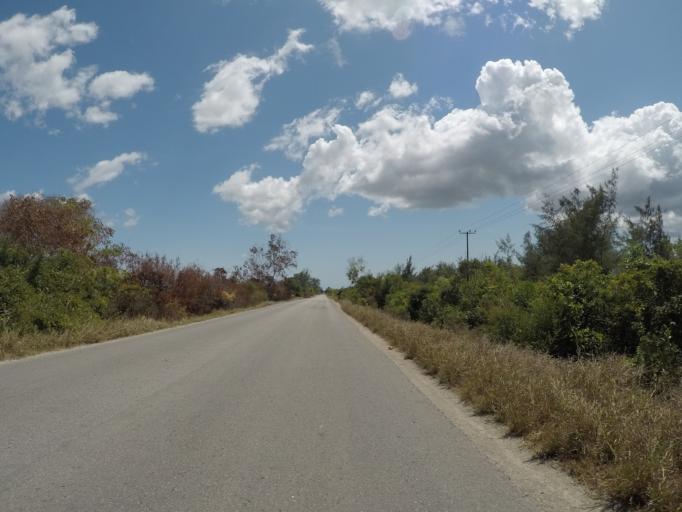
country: TZ
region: Zanzibar Central/South
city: Nganane
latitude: -6.2702
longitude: 39.5089
